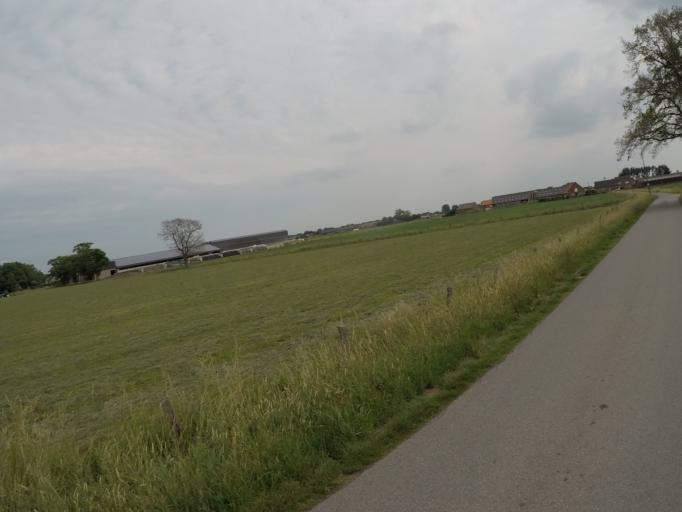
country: BE
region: Flanders
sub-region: Provincie Antwerpen
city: Wuustwezel
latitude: 51.4034
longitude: 4.5790
